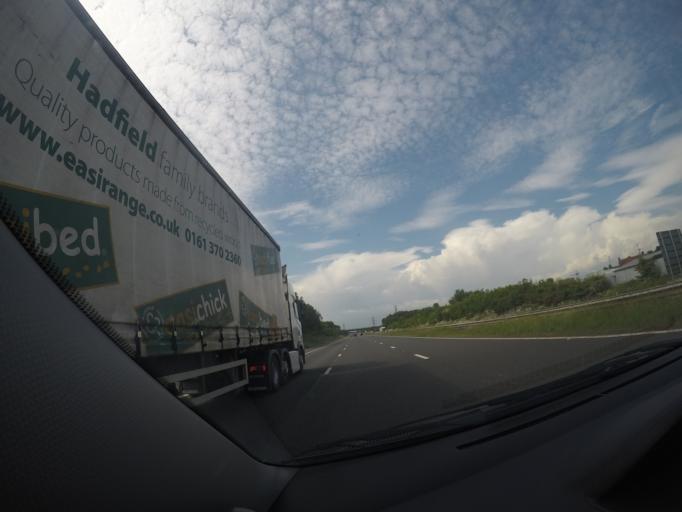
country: GB
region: England
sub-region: Cumbria
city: Carlisle
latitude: 54.9369
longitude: -2.9630
